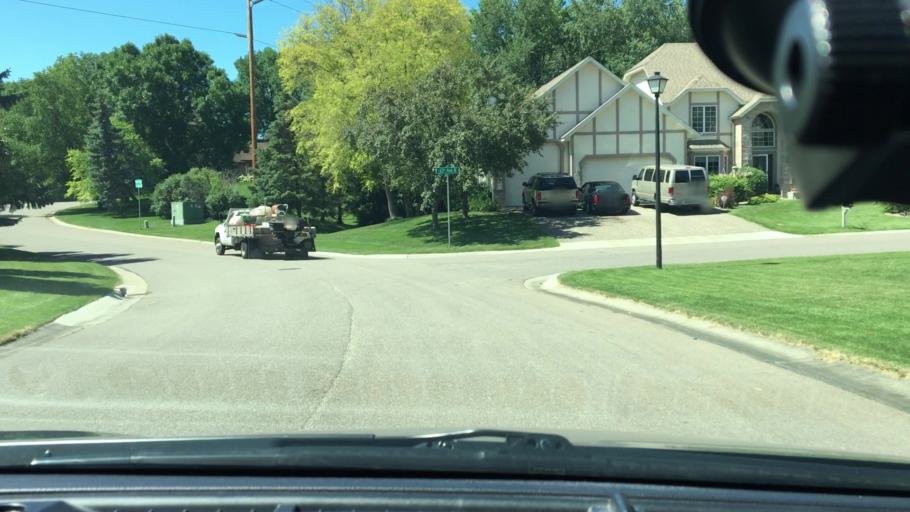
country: US
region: Minnesota
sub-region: Hennepin County
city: Maple Grove
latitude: 45.0685
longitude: -93.4609
